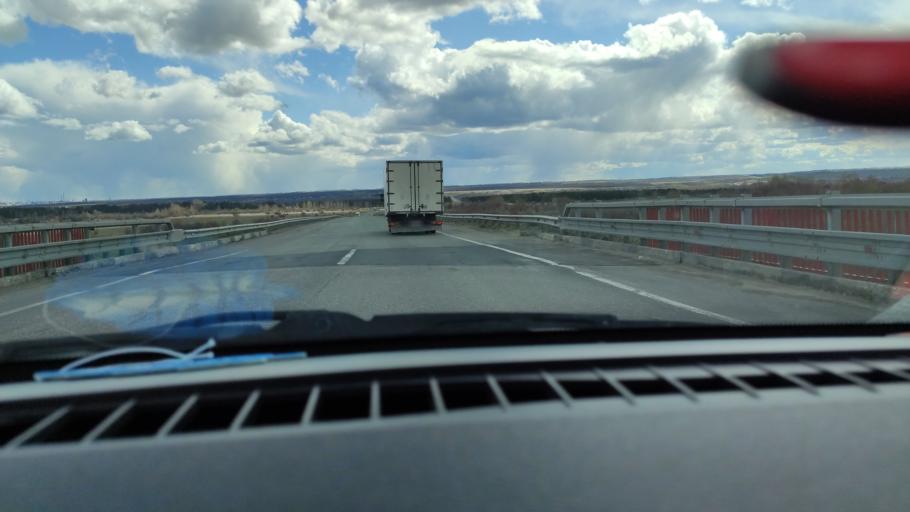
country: RU
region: Samara
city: Varlamovo
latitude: 53.1602
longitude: 48.2837
